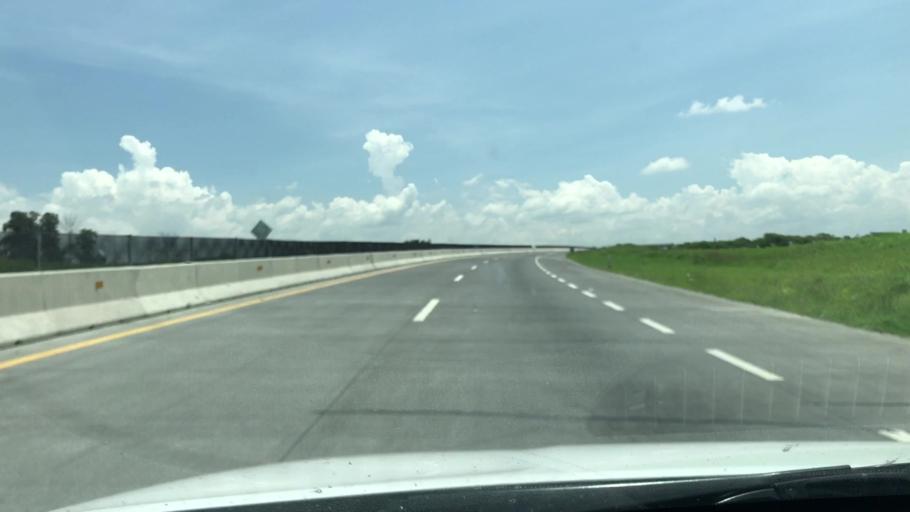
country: MX
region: Jalisco
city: Degollado
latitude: 20.3832
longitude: -102.1184
